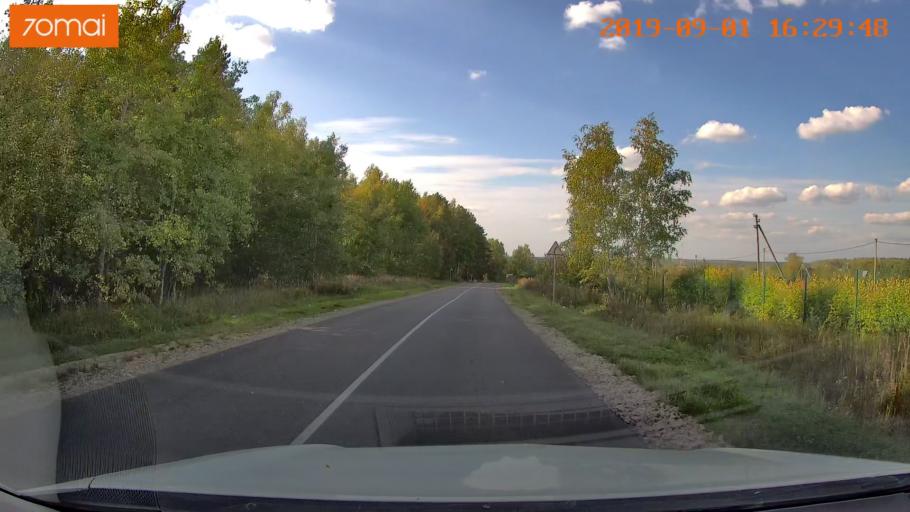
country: RU
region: Kaluga
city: Maloyaroslavets
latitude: 54.9387
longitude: 36.4617
